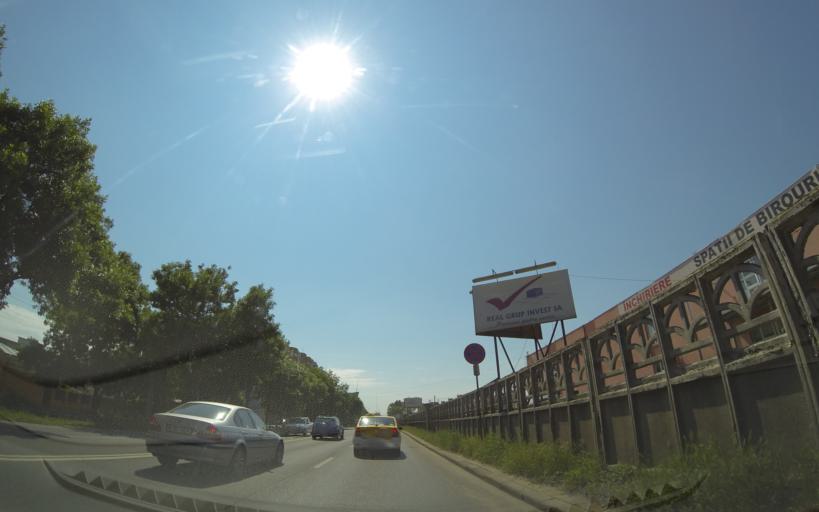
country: RO
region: Bucuresti
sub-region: Municipiul Bucuresti
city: Bucuresti
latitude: 44.4174
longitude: 26.0762
